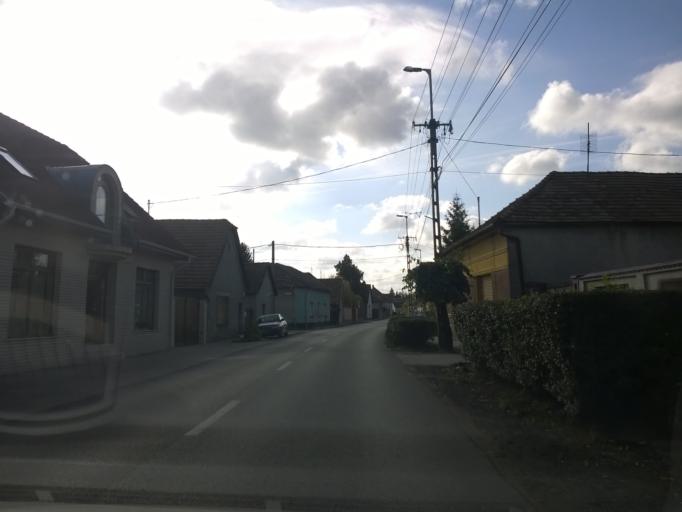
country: HU
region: Pest
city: Rackeve
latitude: 47.1557
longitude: 18.9449
